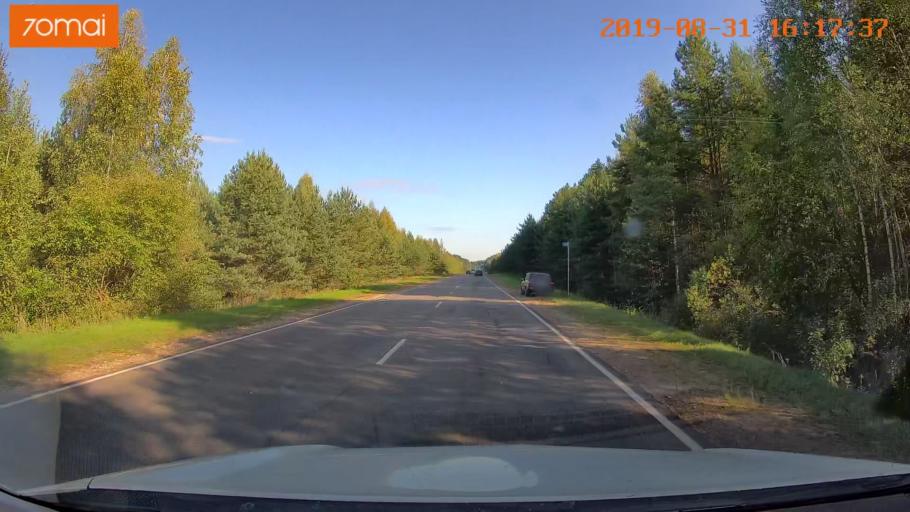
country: RU
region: Kaluga
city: Nikola-Lenivets
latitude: 54.5438
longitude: 35.5384
